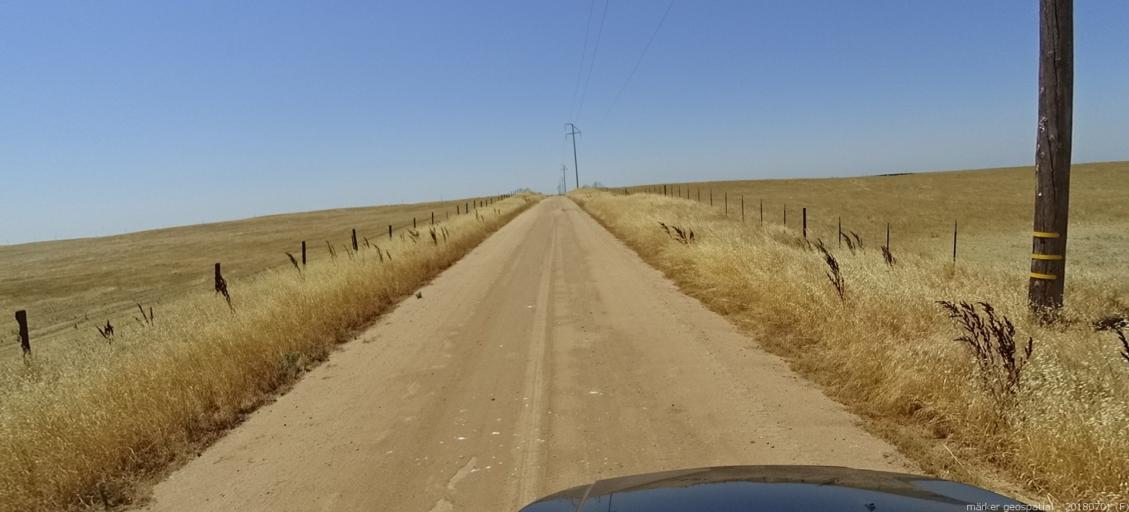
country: US
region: California
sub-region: Madera County
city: Madera Acres
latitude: 37.1089
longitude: -120.0203
